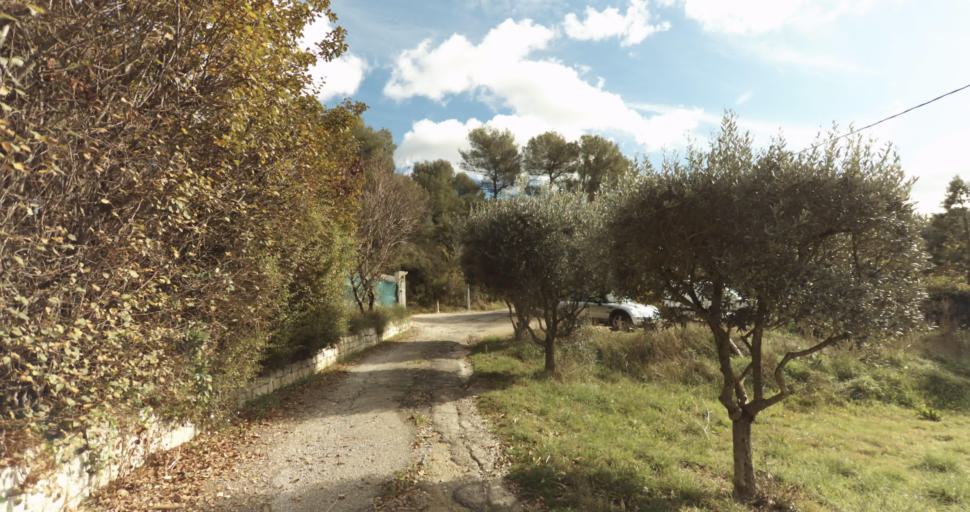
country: FR
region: Provence-Alpes-Cote d'Azur
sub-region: Departement des Bouches-du-Rhone
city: Venelles
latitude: 43.6124
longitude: 5.4916
